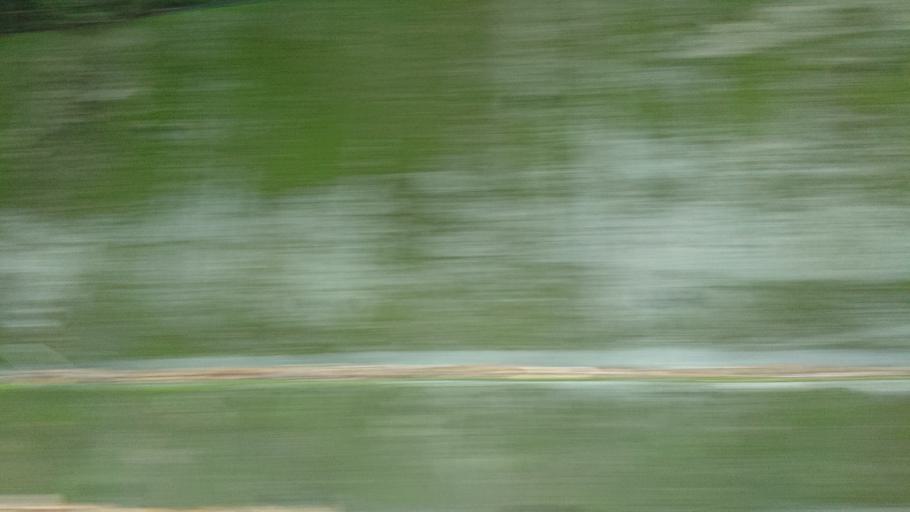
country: TW
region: Taiwan
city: Daxi
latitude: 24.8742
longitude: 121.3864
